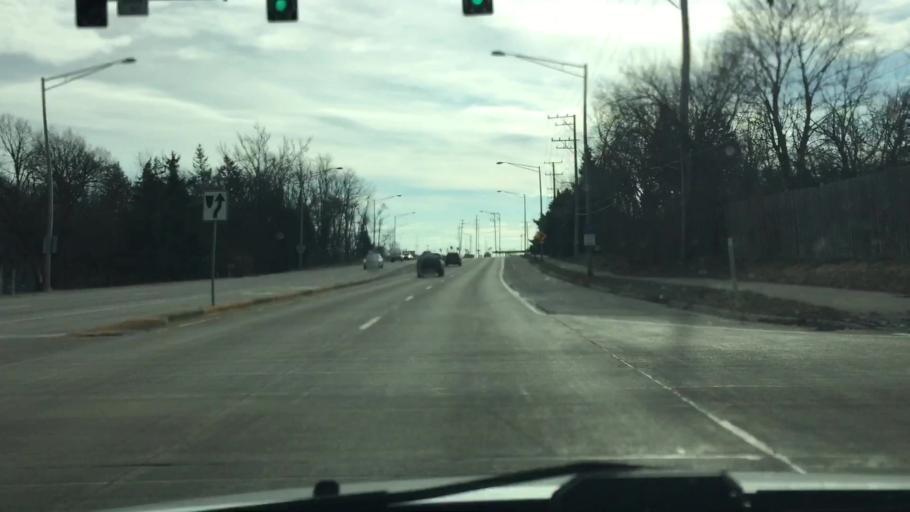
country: US
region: Illinois
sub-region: Kane County
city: Geneva
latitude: 41.8905
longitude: -88.2772
